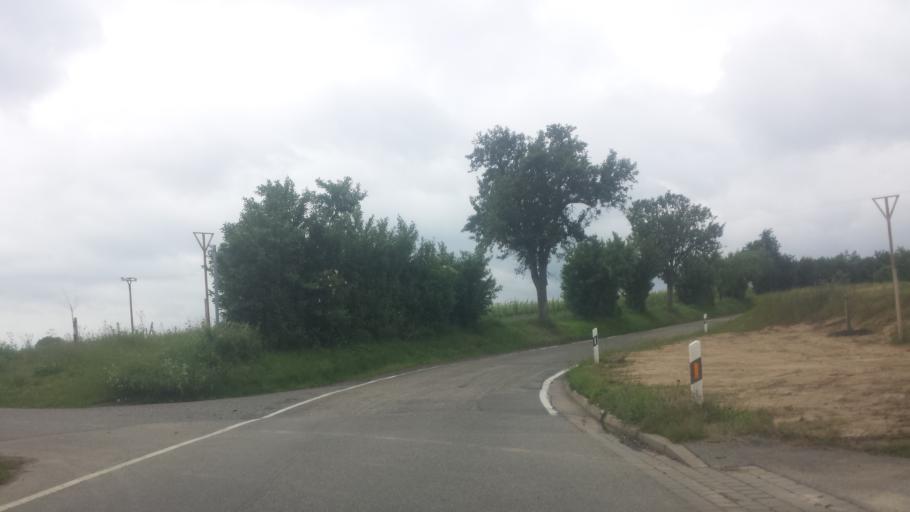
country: DE
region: Rheinland-Pfalz
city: Impflingen
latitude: 49.1646
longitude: 8.1095
